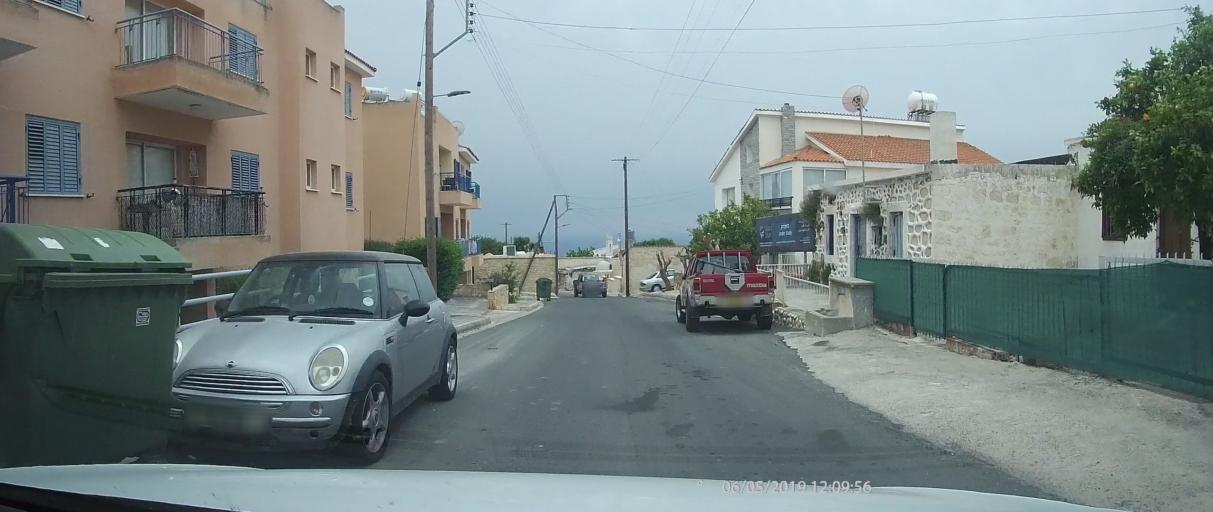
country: CY
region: Pafos
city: Tala
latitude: 34.8382
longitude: 32.4335
